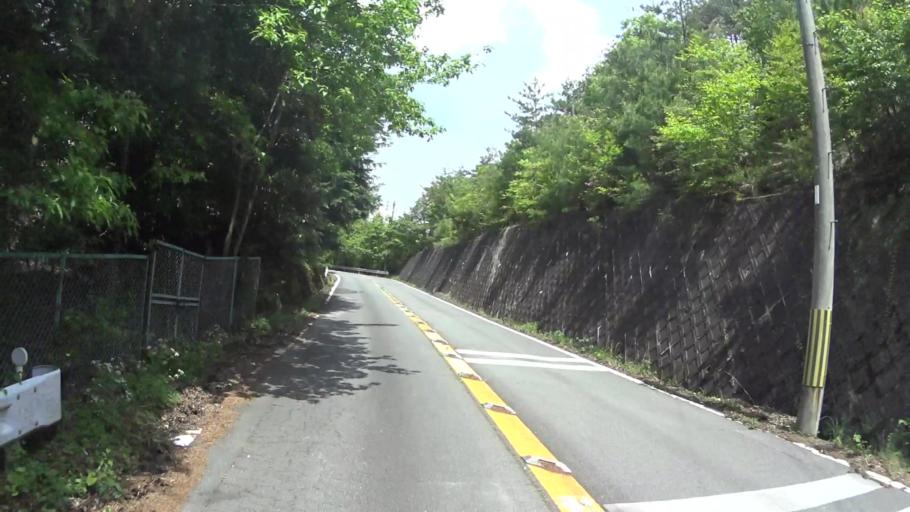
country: JP
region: Kyoto
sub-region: Kyoto-shi
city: Kamigyo-ku
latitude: 35.0628
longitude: 135.7242
